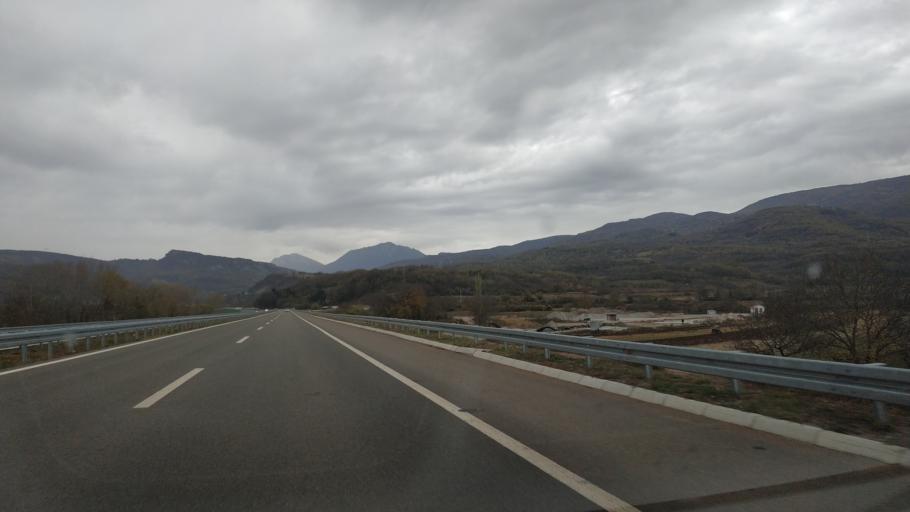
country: RS
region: Central Serbia
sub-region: Nisavski Okrug
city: Niska Banja
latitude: 43.3069
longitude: 22.0386
